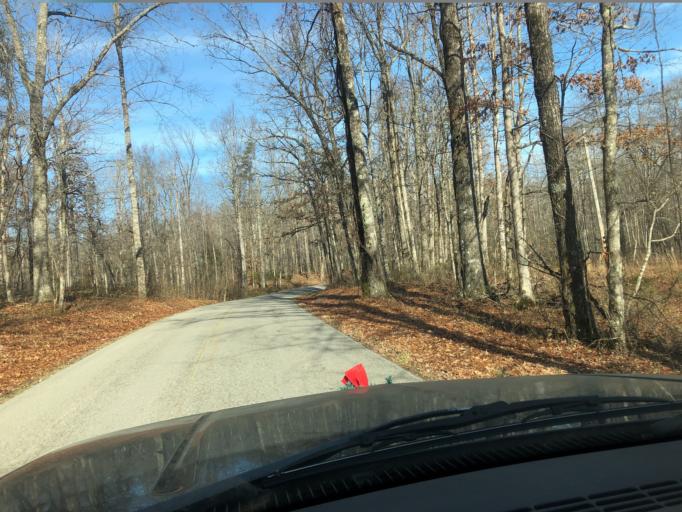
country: US
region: Tennessee
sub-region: Putnam County
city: Monterey
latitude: 35.9912
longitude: -85.2808
